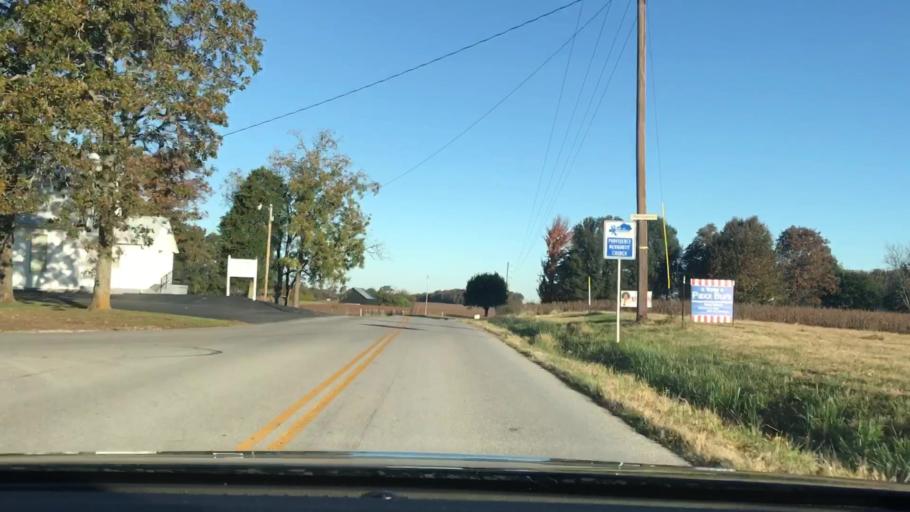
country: US
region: Kentucky
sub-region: Logan County
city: Auburn
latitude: 36.8064
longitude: -86.6365
